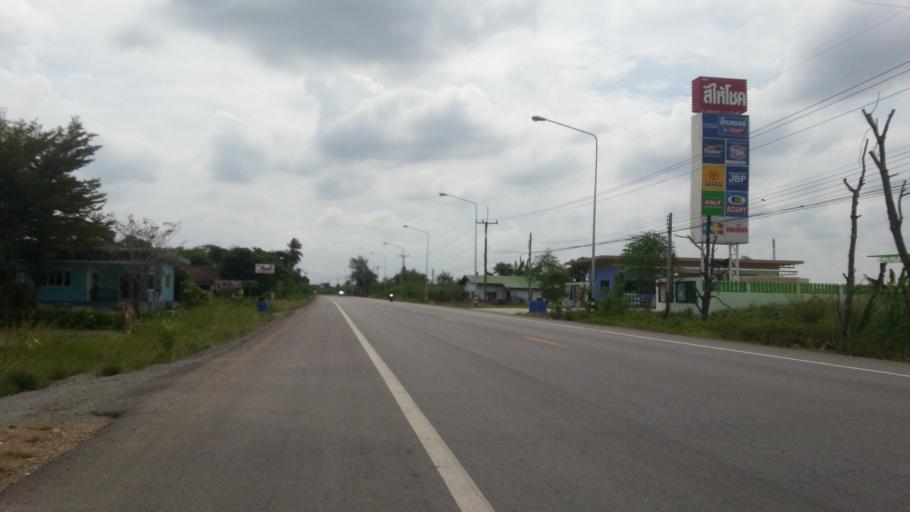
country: TH
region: Pathum Thani
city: Ban Rangsit
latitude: 14.0410
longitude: 100.8443
